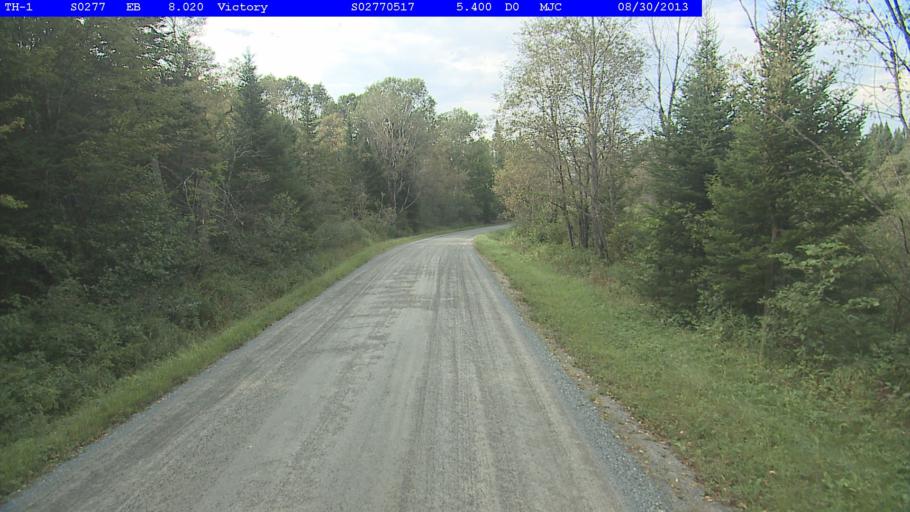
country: US
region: Vermont
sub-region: Caledonia County
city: Lyndonville
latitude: 44.5467
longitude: -71.7850
